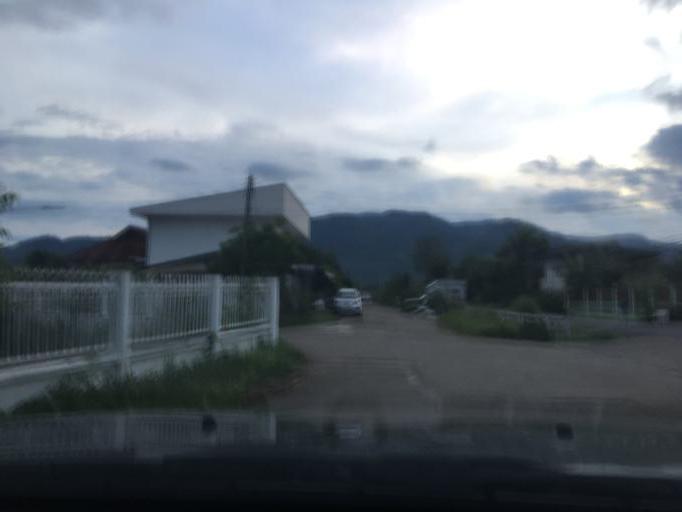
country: TH
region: Chiang Mai
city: Chiang Mai
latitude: 18.8684
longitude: 98.9673
